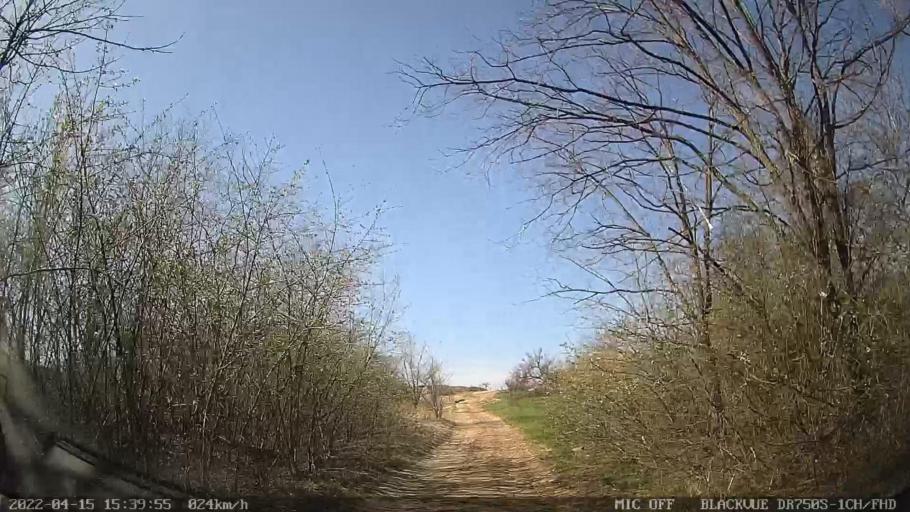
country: MD
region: Raionul Ocnita
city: Otaci
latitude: 48.3546
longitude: 27.9263
